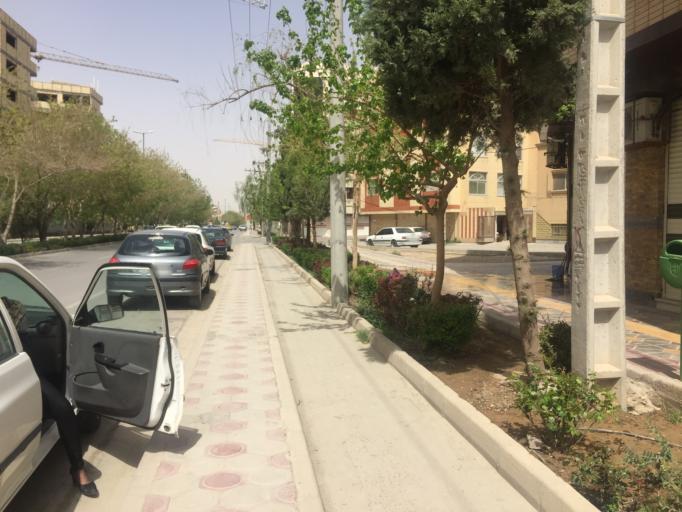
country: IR
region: Isfahan
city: Isfahan
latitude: 32.6994
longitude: 51.6793
